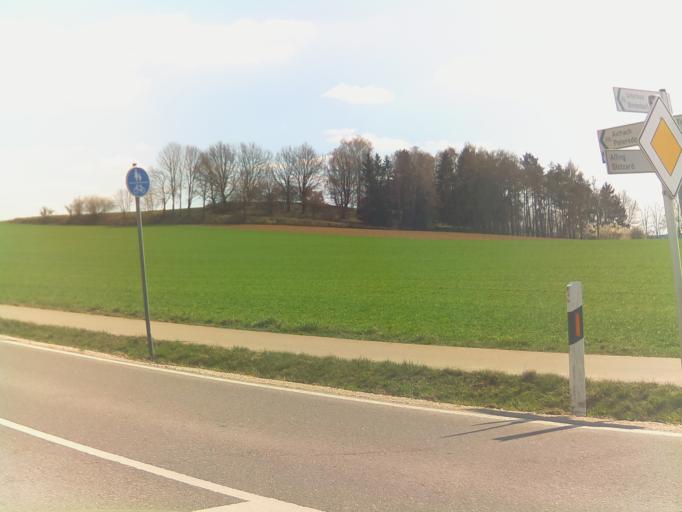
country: DE
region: Bavaria
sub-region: Swabia
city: Aindling
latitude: 48.5123
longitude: 10.9777
